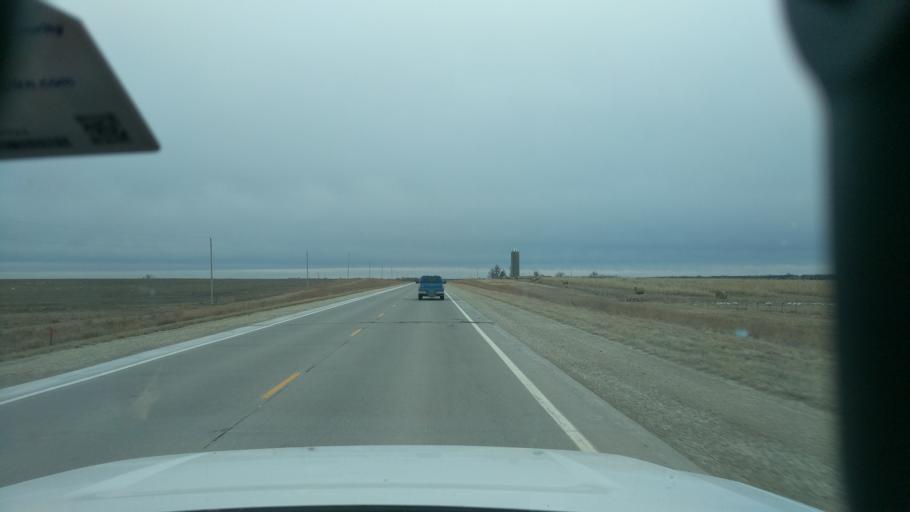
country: US
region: Kansas
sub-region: Dickinson County
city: Herington
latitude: 38.5801
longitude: -96.9482
